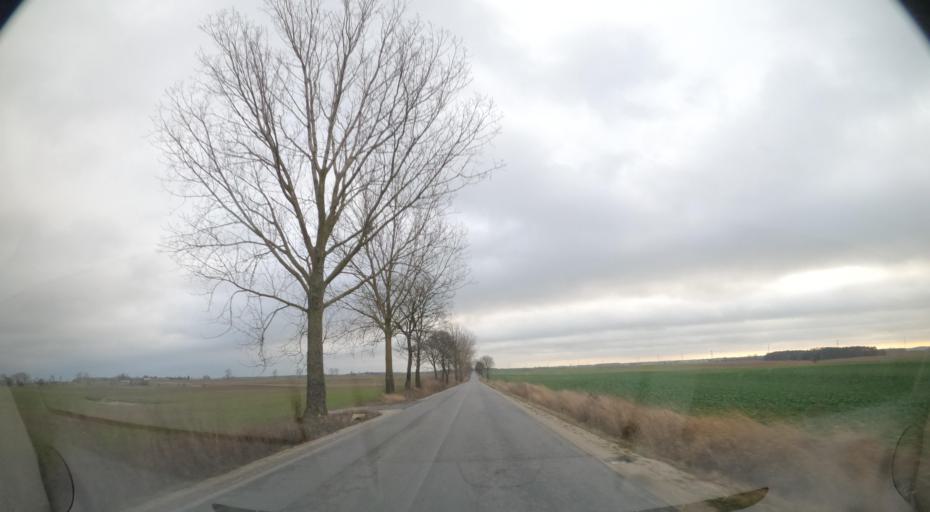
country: PL
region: Kujawsko-Pomorskie
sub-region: Powiat nakielski
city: Sadki
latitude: 53.2067
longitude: 17.3683
